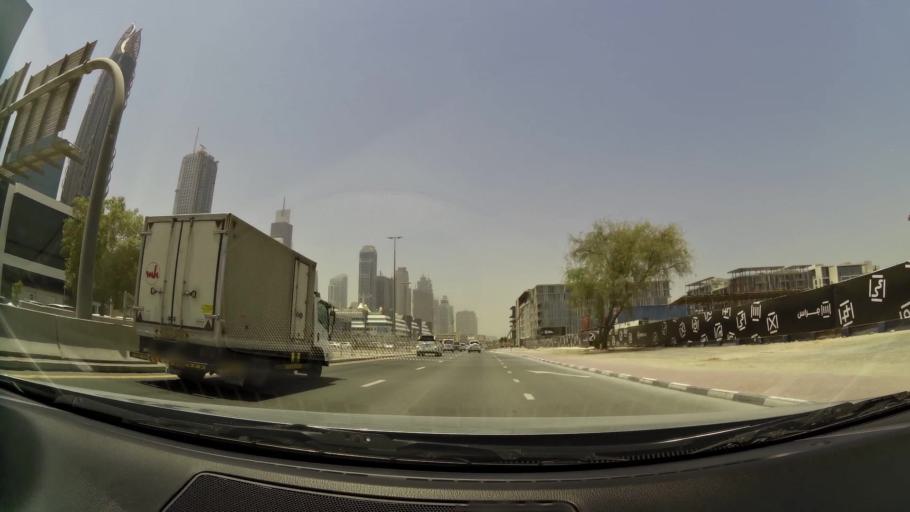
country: AE
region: Dubai
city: Dubai
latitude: 25.2026
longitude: 55.2666
